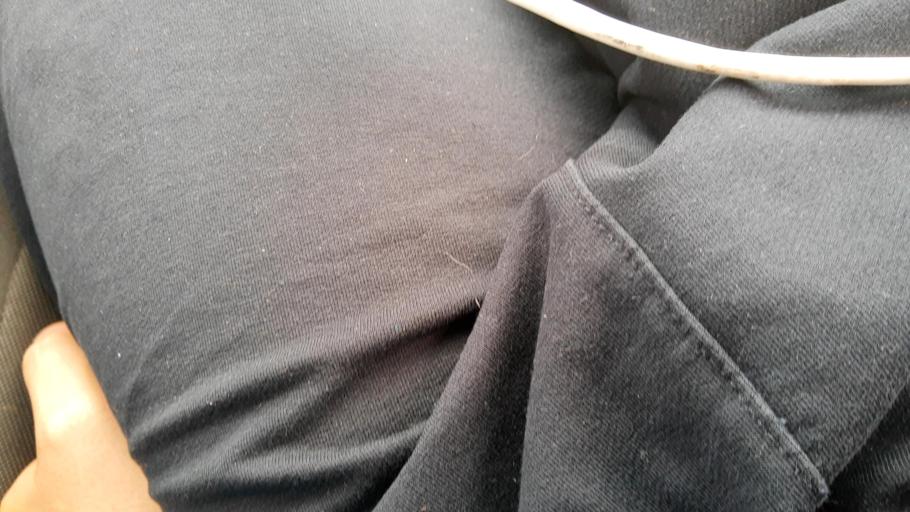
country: RU
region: Bashkortostan
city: Pavlovka
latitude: 55.3981
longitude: 56.4524
